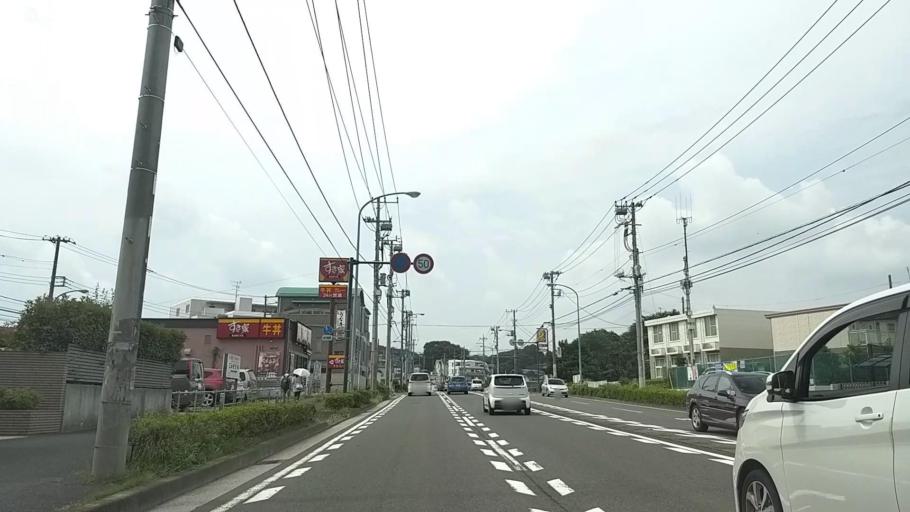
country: JP
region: Kanagawa
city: Minami-rinkan
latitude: 35.5092
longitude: 139.5446
